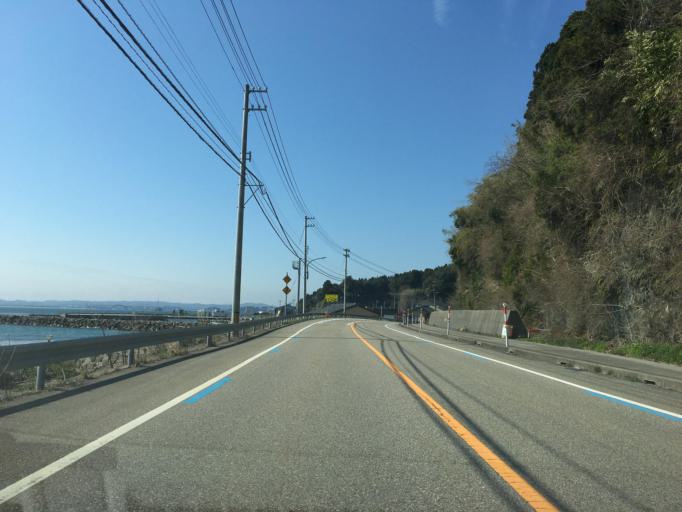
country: JP
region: Toyama
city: Himi
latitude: 36.8982
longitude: 137.0091
